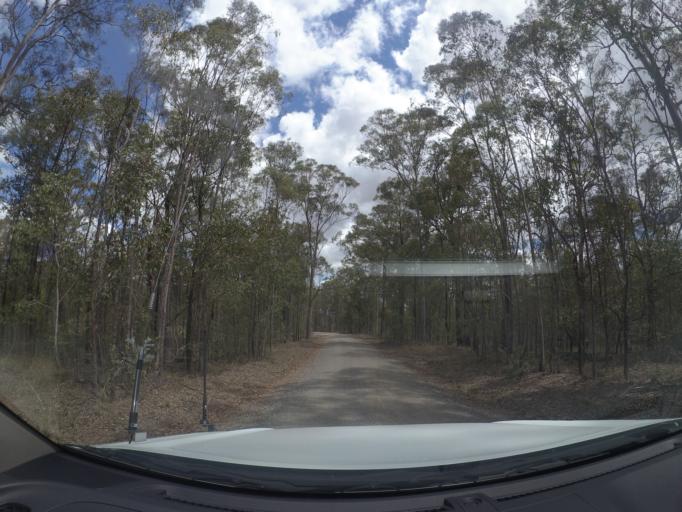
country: AU
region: Queensland
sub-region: Logan
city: Cedar Vale
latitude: -27.9057
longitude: 153.0312
